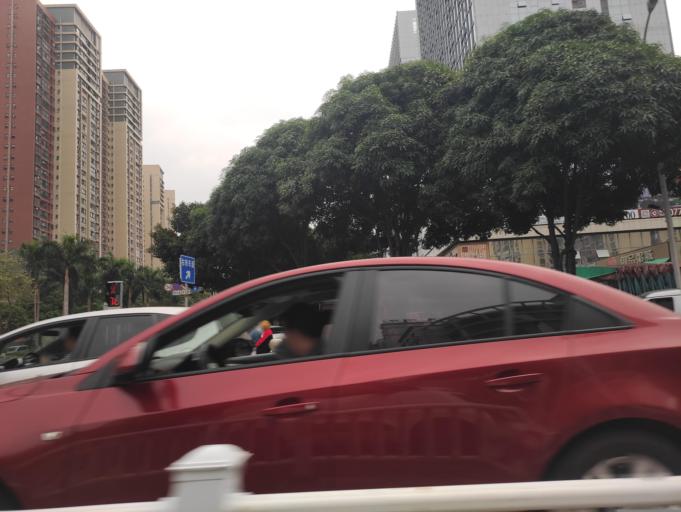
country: CN
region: Guangxi Zhuangzu Zizhiqu
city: Baise City
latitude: 23.8921
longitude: 106.6303
